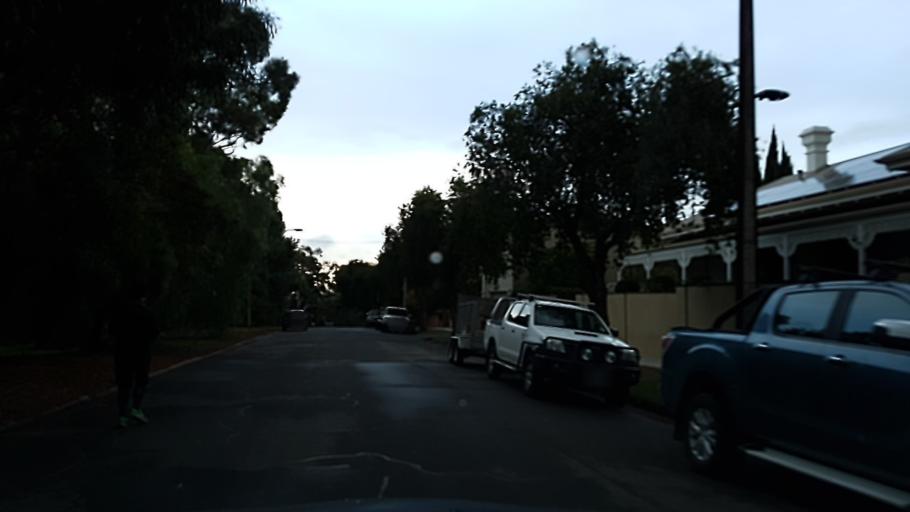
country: AU
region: South Australia
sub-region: Adelaide
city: North Adelaide
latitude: -34.9069
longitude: 138.5849
